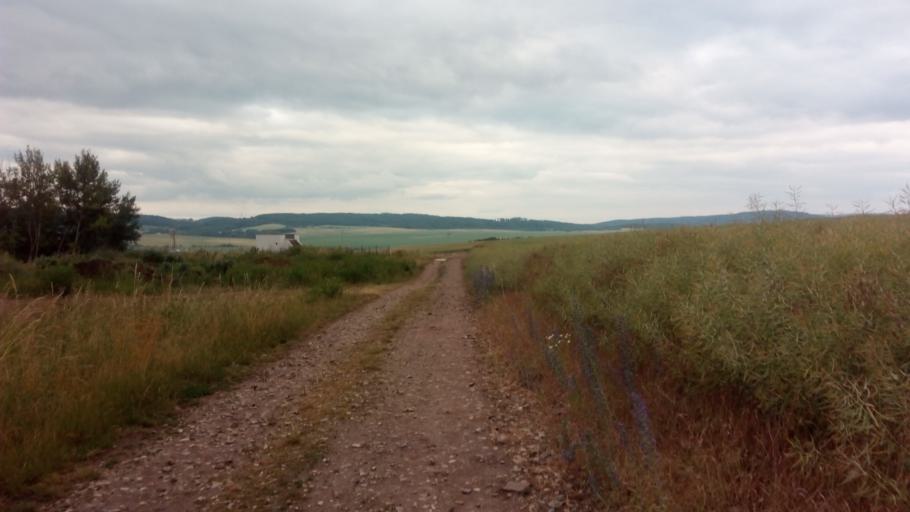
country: CZ
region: South Moravian
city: Ricany
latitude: 49.2099
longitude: 16.3877
